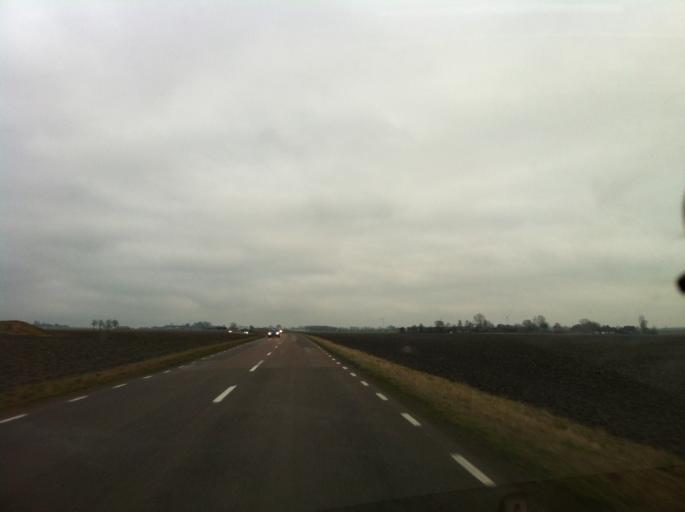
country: SE
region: Skane
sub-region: Landskrona
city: Landskrona
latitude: 55.9029
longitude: 12.8496
